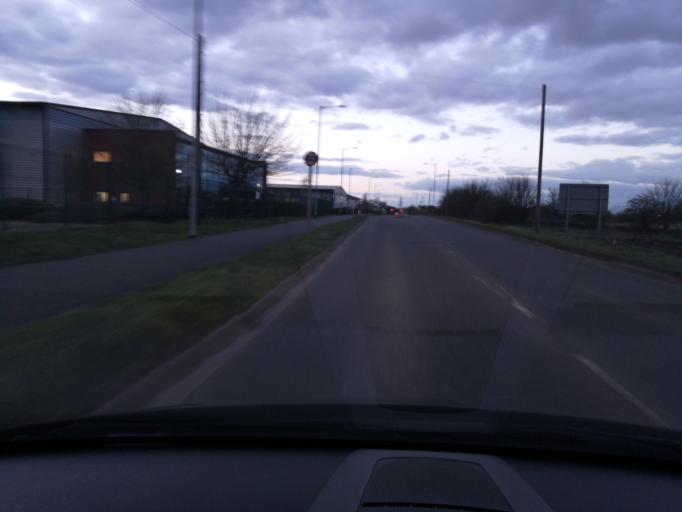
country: GB
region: England
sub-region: Peterborough
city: Eye
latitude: 52.5812
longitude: -0.2039
